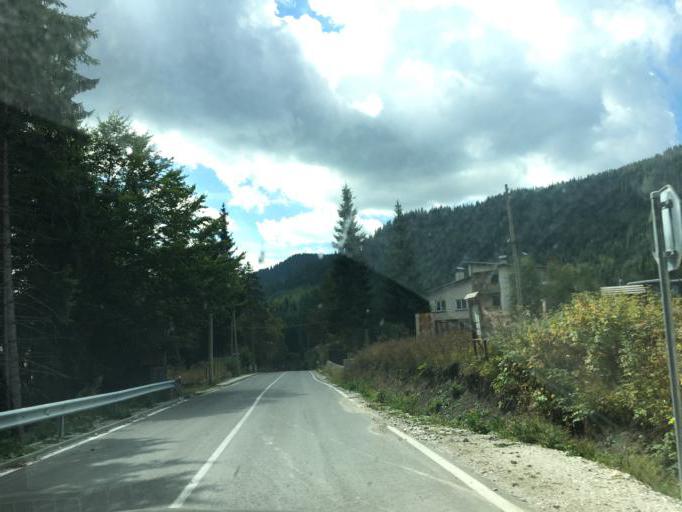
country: BG
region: Pazardzhik
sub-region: Obshtina Batak
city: Batak
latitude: 41.9072
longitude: 24.2980
